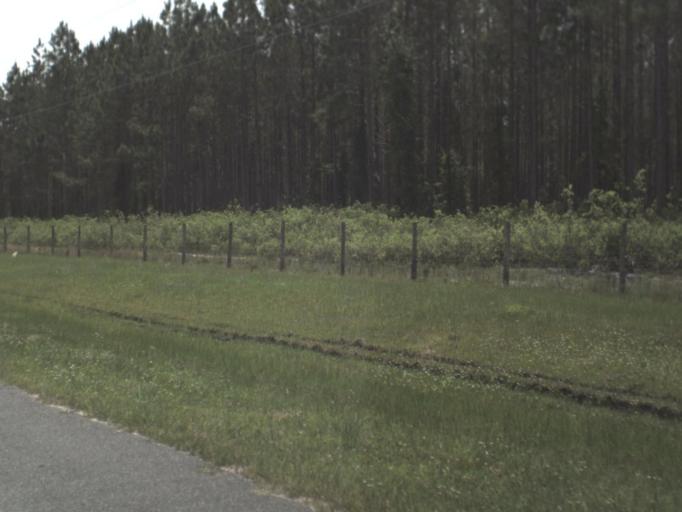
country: US
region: Florida
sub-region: Clay County
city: Asbury Lake
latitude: 29.9255
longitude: -81.8974
